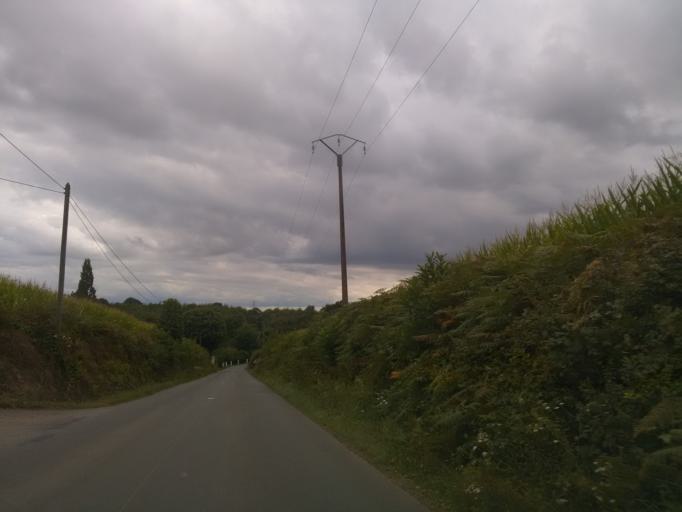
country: FR
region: Brittany
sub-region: Departement d'Ille-et-Vilaine
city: Vignoc
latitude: 48.2415
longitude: -1.7879
